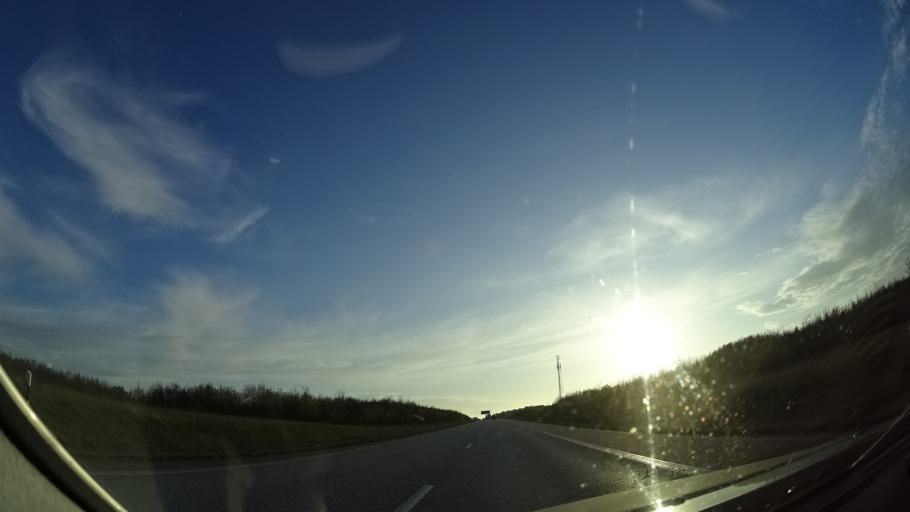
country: SE
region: Skane
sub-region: Malmo
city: Tygelsjo
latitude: 55.5499
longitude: 13.0305
